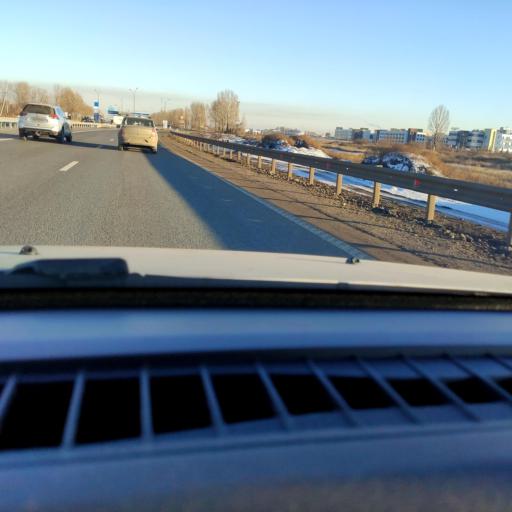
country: RU
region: Samara
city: Podstepki
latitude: 53.5601
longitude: 49.2094
